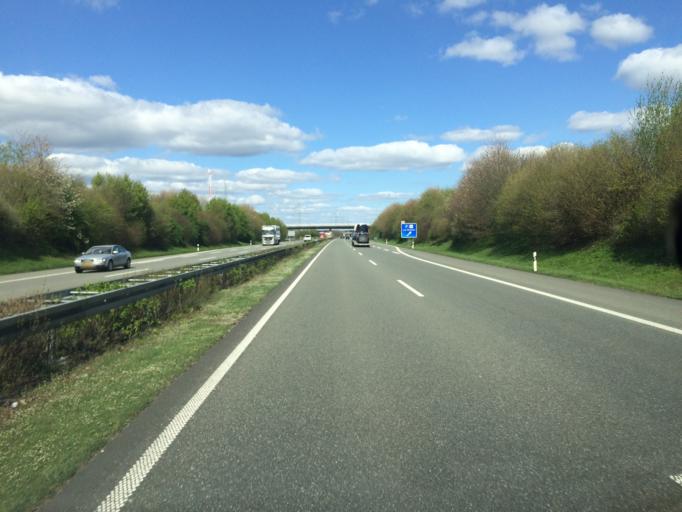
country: DE
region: North Rhine-Westphalia
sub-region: Regierungsbezirk Munster
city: Ochtrup
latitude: 52.2210
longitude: 7.1356
